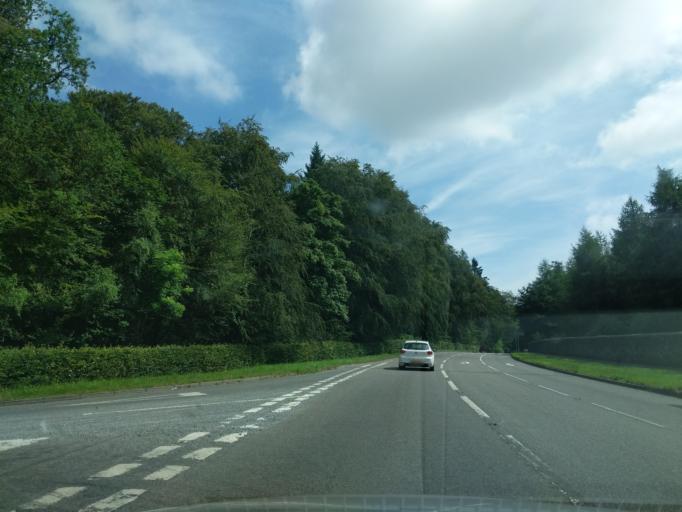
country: GB
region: Scotland
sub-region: Angus
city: Muirhead
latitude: 56.4908
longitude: -3.0445
